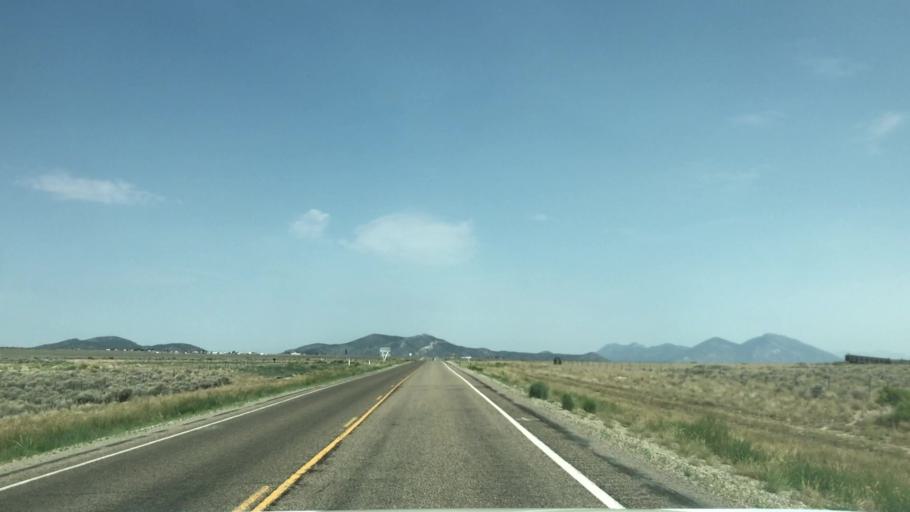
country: US
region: Nevada
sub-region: White Pine County
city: Ely
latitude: 39.1798
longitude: -114.8272
